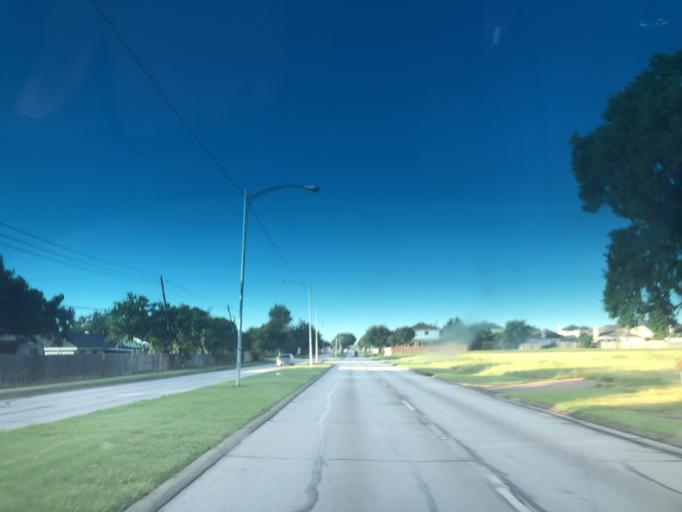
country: US
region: Texas
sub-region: Dallas County
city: Grand Prairie
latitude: 32.7032
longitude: -97.0155
